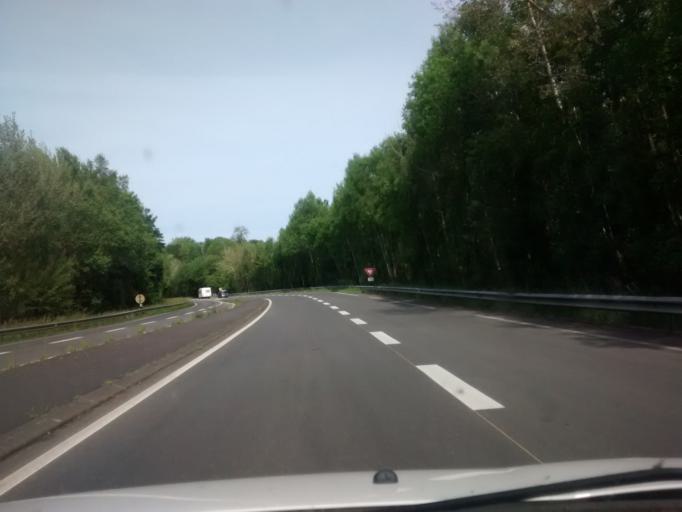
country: FR
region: Brittany
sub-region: Departement d'Ille-et-Vilaine
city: Antrain
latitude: 48.4591
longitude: -1.4952
